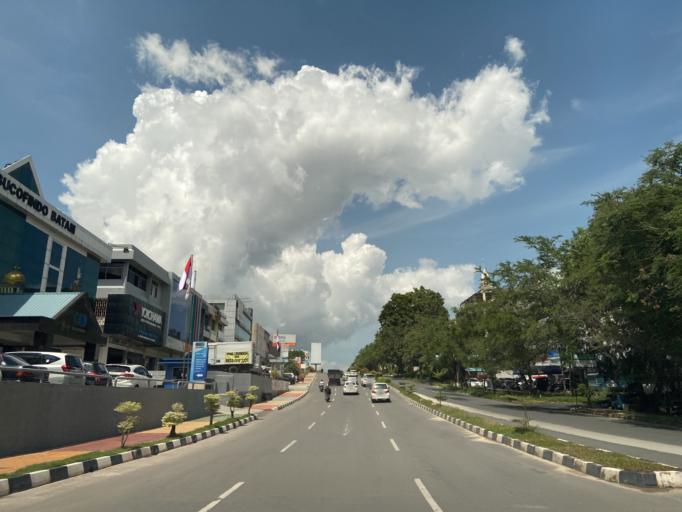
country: SG
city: Singapore
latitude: 1.1374
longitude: 104.0165
